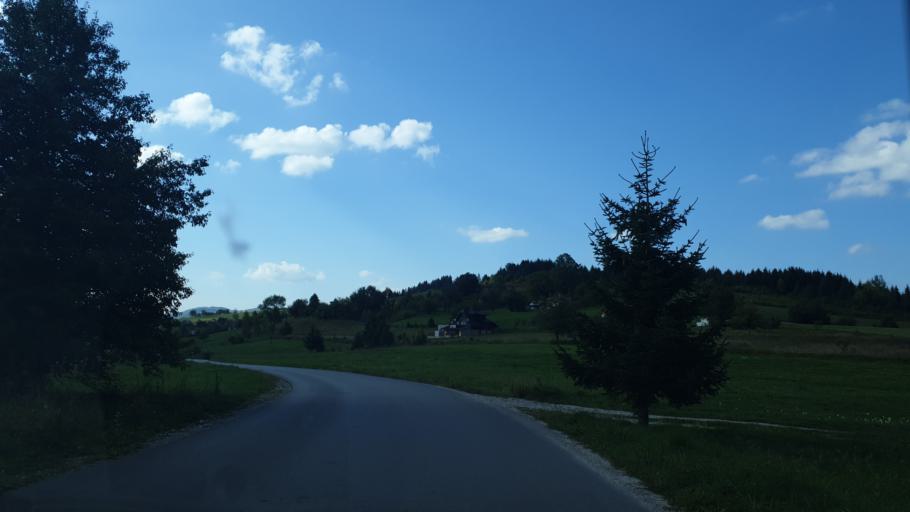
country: RS
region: Central Serbia
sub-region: Zlatiborski Okrug
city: Nova Varos
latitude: 43.4361
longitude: 19.8719
